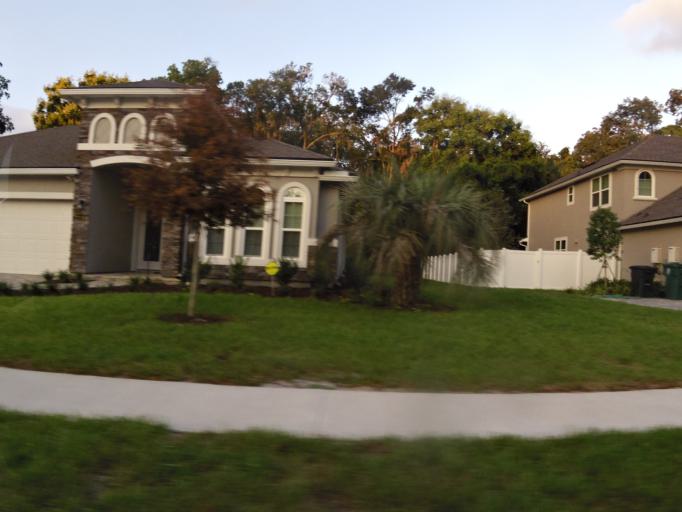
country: US
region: Florida
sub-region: Clay County
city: Orange Park
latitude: 30.1871
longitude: -81.6358
